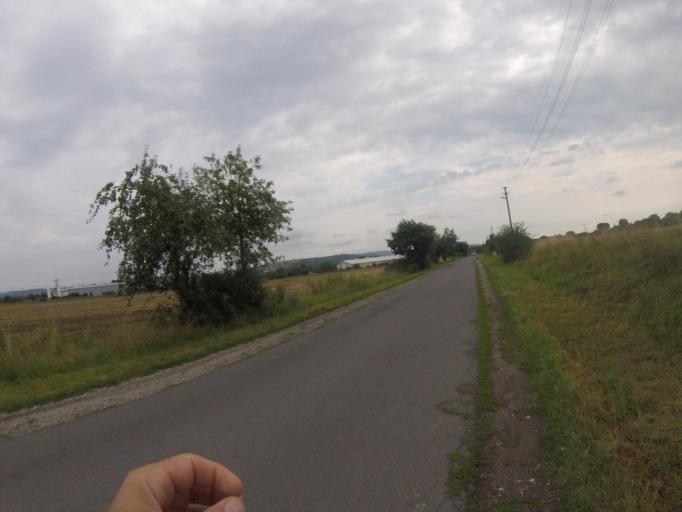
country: SK
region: Nitriansky
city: Sahy
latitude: 48.0595
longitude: 18.9425
